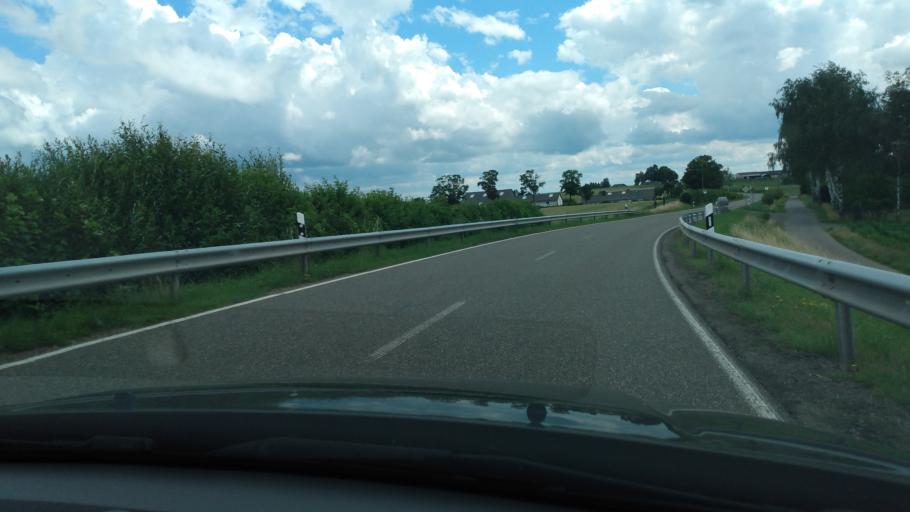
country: DE
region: Rheinland-Pfalz
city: Manderscheid
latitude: 50.1027
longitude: 6.7989
